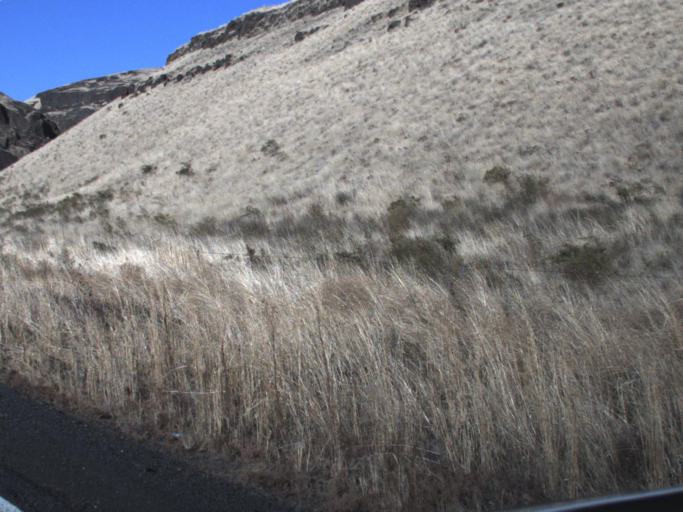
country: US
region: Washington
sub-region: Franklin County
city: Connell
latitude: 46.5897
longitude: -118.5443
